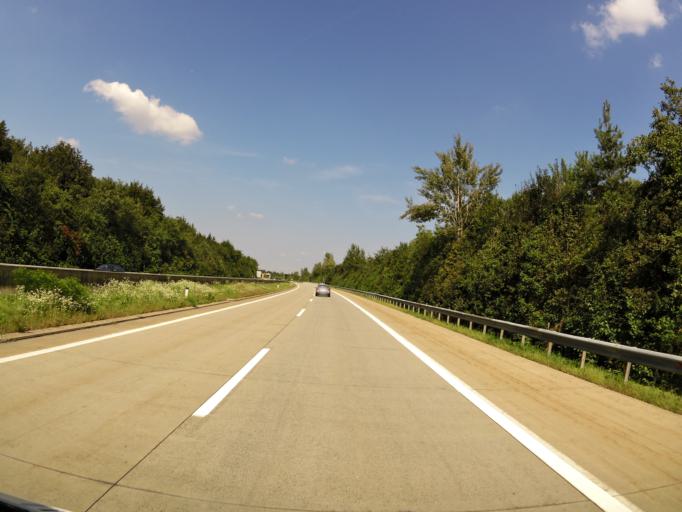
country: AT
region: Styria
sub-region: Politischer Bezirk Leibnitz
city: Spielfeld
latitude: 46.7169
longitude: 15.6474
